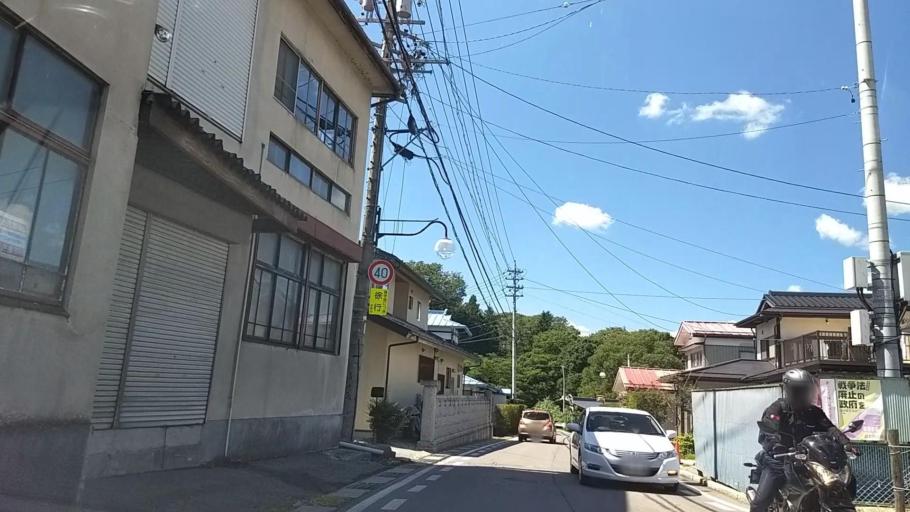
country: JP
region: Nagano
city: Chino
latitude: 36.0304
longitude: 138.2272
